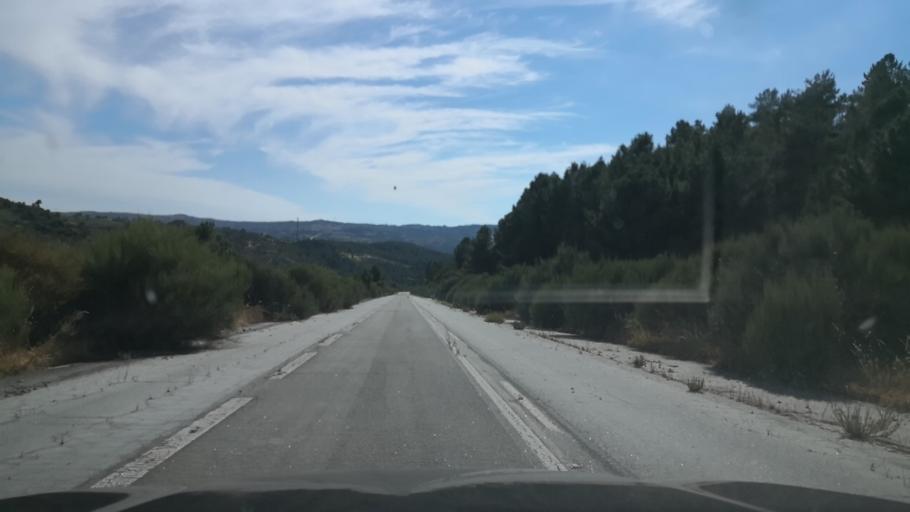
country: PT
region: Vila Real
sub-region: Sabrosa
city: Sabrosa
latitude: 41.3618
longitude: -7.5579
